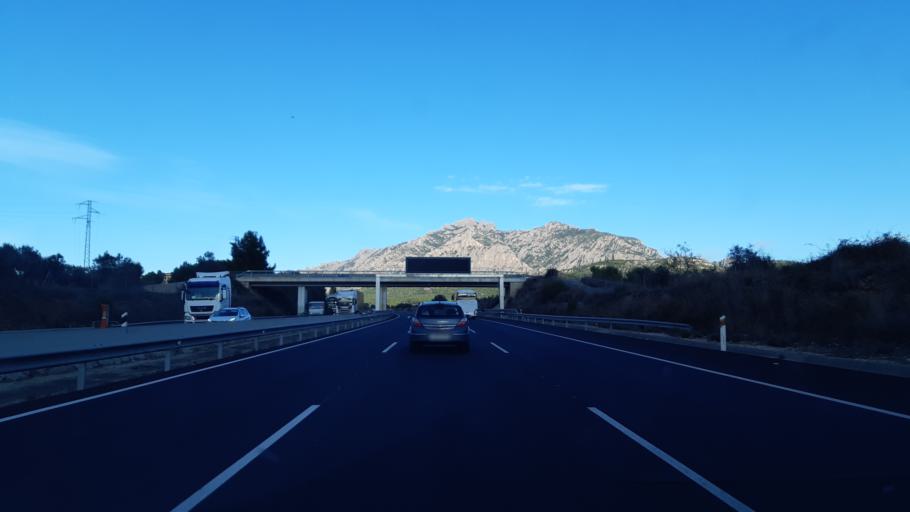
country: ES
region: Catalonia
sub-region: Provincia de Barcelona
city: Esparreguera
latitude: 41.5433
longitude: 1.8554
